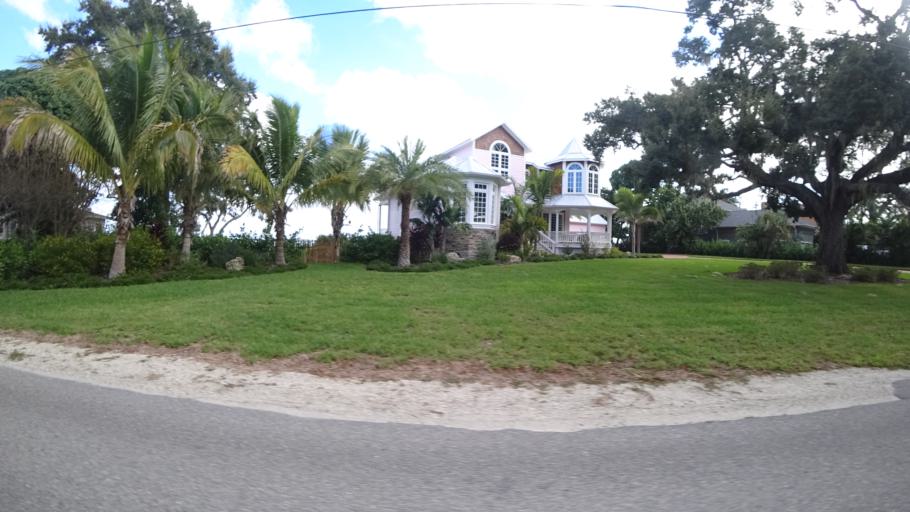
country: US
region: Florida
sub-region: Manatee County
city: West Bradenton
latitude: 27.5082
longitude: -82.6151
